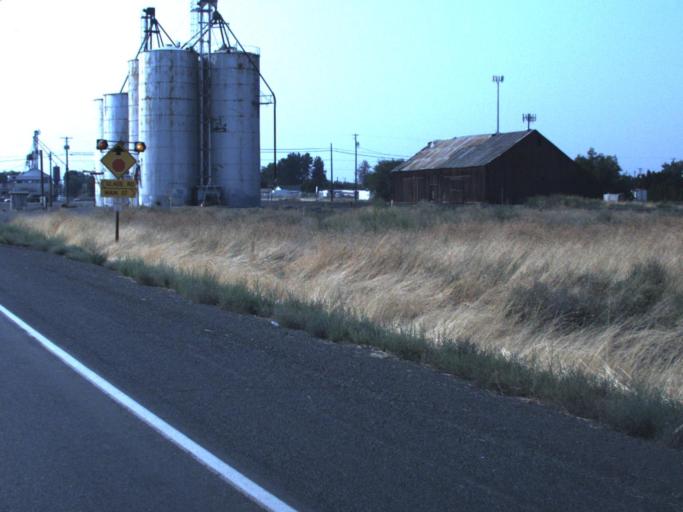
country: US
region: Washington
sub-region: Yakima County
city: Mabton
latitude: 46.2106
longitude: -119.9960
